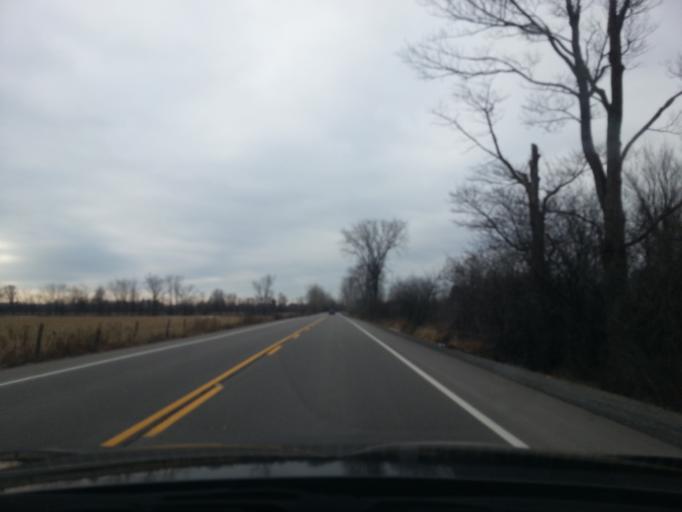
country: CA
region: Ontario
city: Ottawa
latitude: 45.4208
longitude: -75.5769
